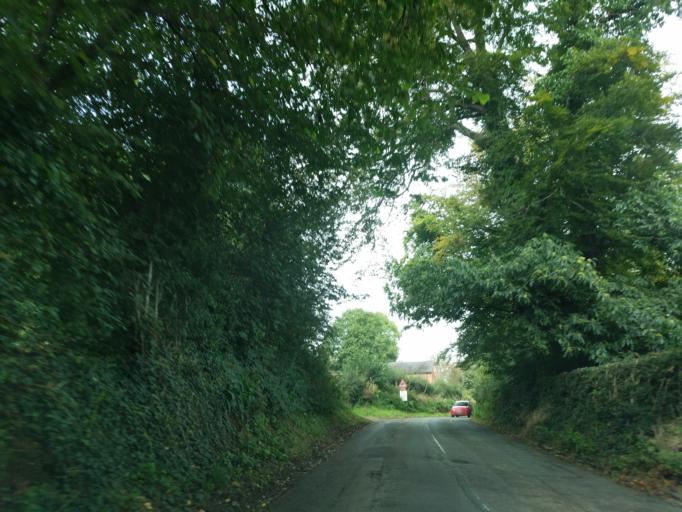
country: GB
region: England
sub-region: Staffordshire
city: Standon
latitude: 52.9701
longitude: -2.2836
